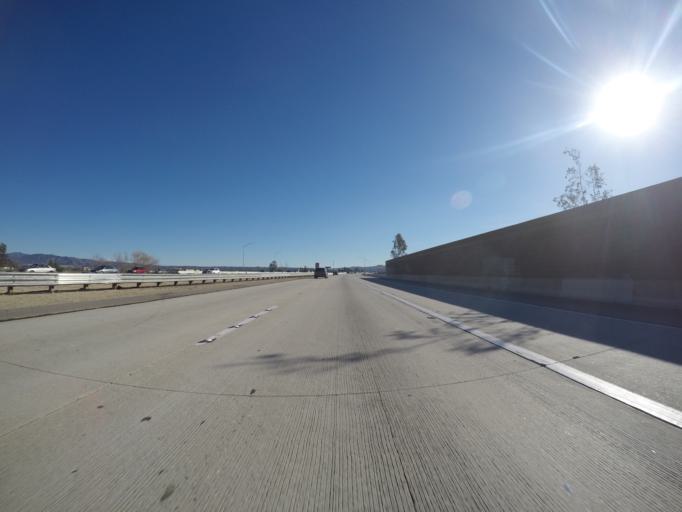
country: US
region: California
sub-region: San Bernardino County
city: Highland
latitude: 34.1136
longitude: -117.2000
